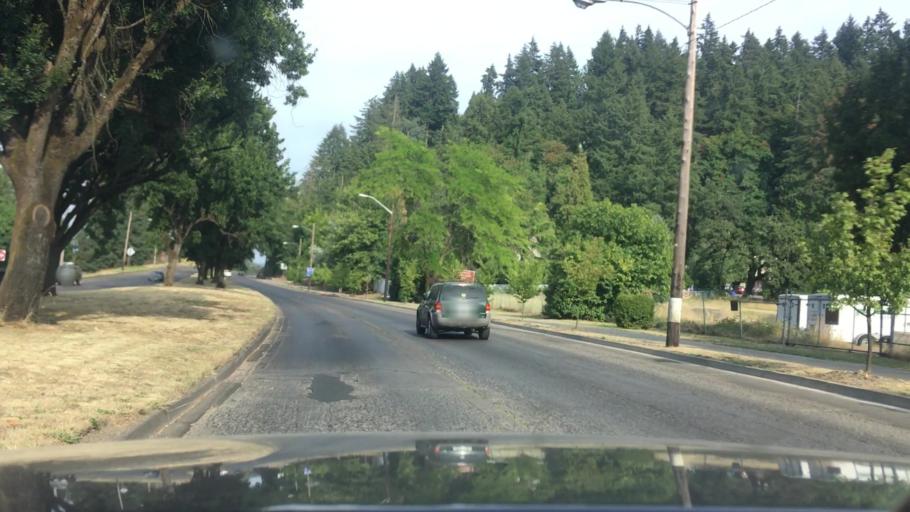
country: US
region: Oregon
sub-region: Lane County
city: Eugene
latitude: 44.0442
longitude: -123.0587
